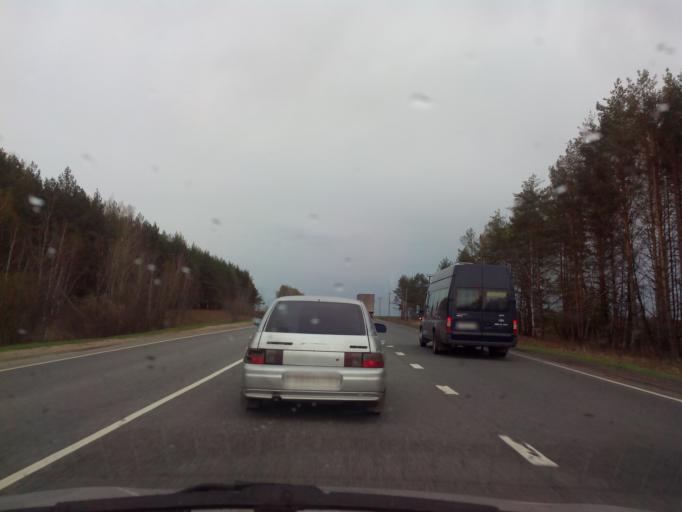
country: RU
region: Moskovskaya
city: Uzunovo
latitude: 54.4992
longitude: 38.5054
